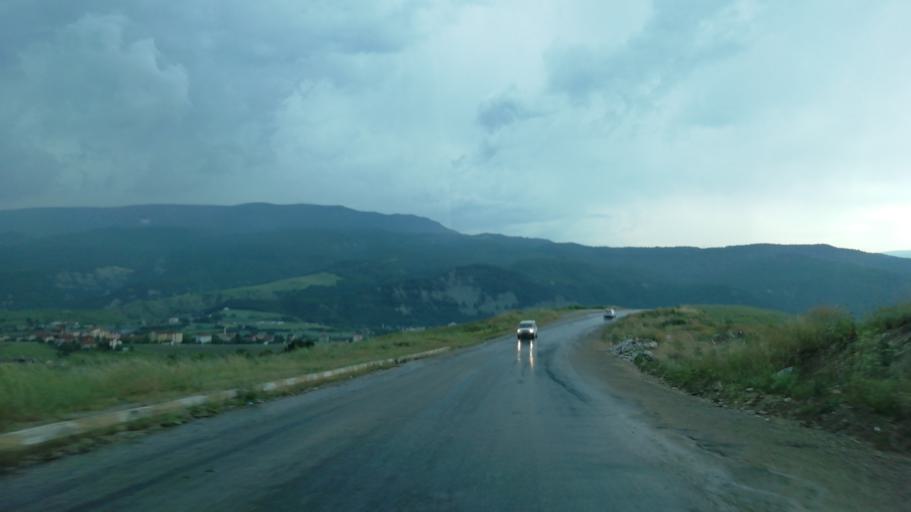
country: TR
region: Karabuk
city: Safranbolu
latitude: 41.2274
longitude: 32.6872
